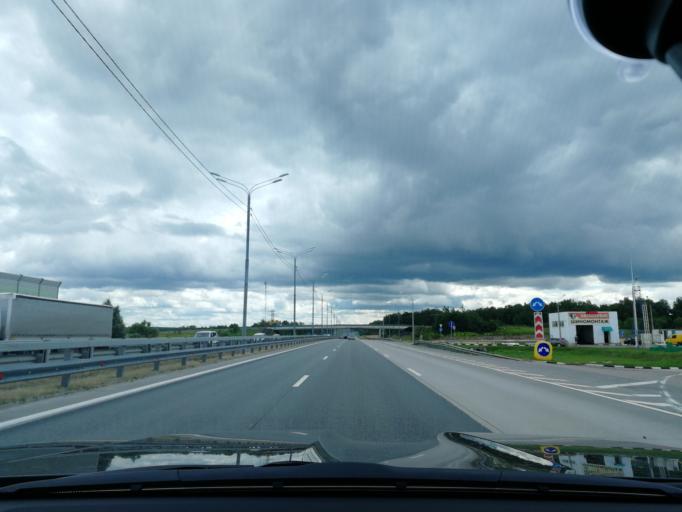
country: RU
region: Moskovskaya
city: Barybino
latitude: 55.2595
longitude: 37.8674
